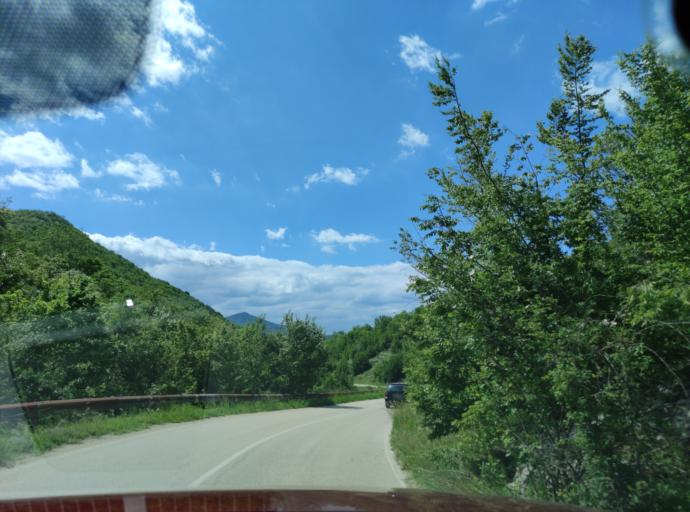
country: BG
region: Vidin
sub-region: Obshtina Ruzhintsi
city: Ruzhintsi
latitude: 43.4928
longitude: 22.8005
